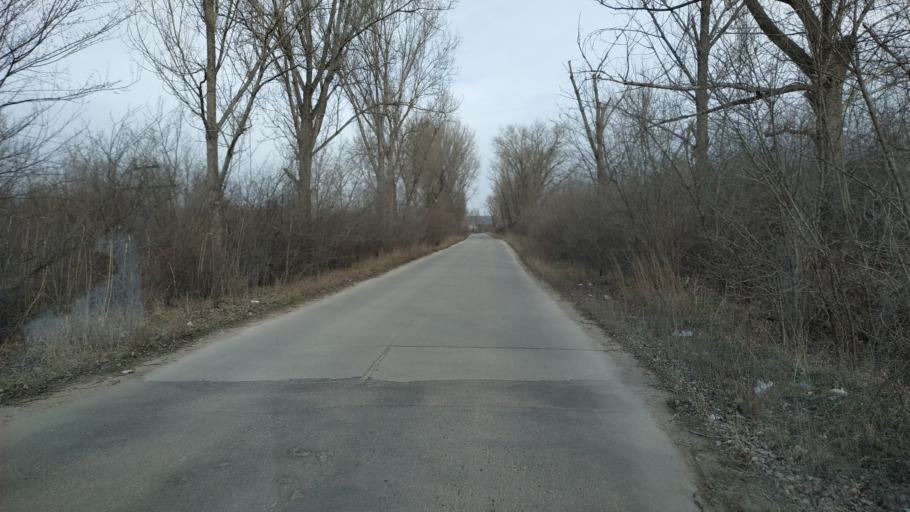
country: MD
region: Chisinau
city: Vatra
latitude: 47.0885
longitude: 28.7399
